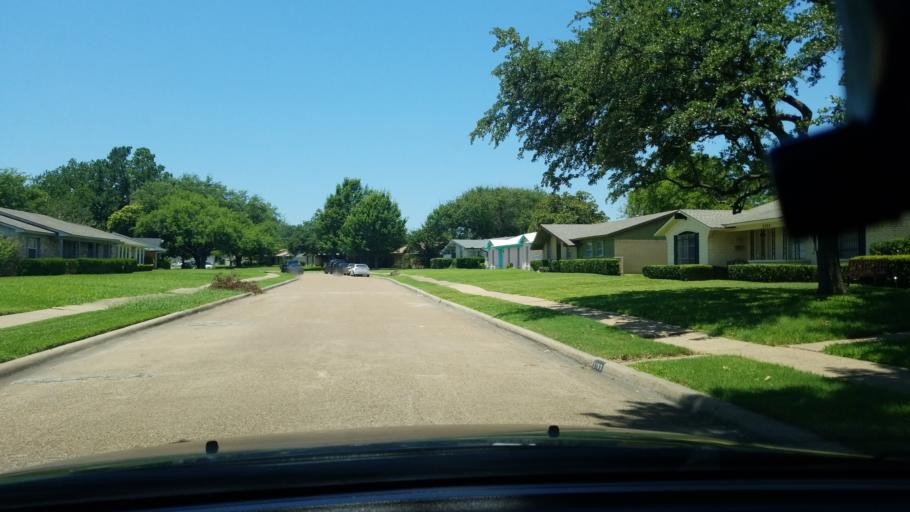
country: US
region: Texas
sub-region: Dallas County
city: Mesquite
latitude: 32.7972
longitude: -96.6484
